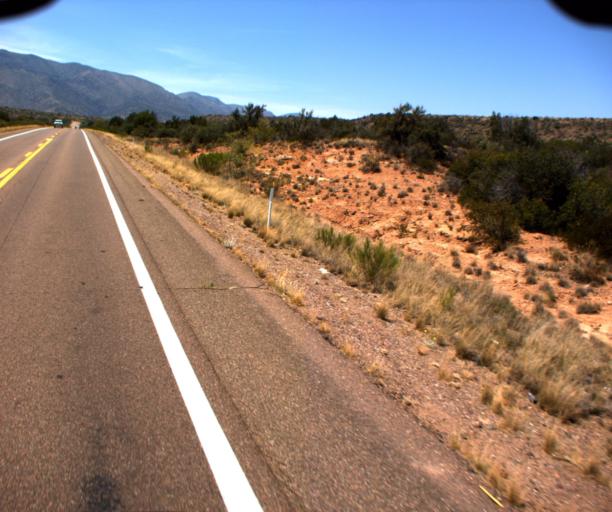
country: US
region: Arizona
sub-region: Gila County
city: Payson
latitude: 34.0290
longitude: -111.3501
